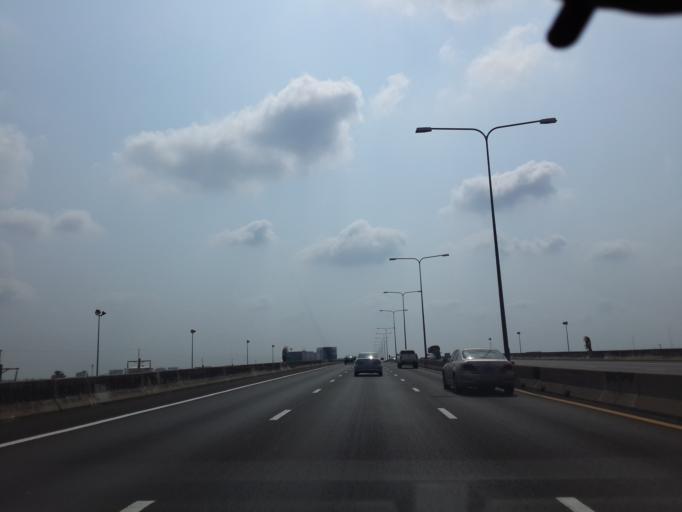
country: TH
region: Bangkok
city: Bang Na
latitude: 13.6403
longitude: 100.6995
